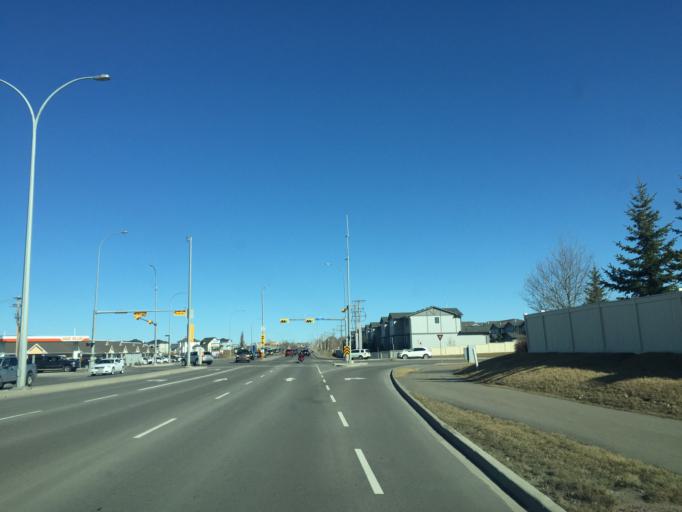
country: CA
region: Alberta
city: Airdrie
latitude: 51.2999
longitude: -114.0265
